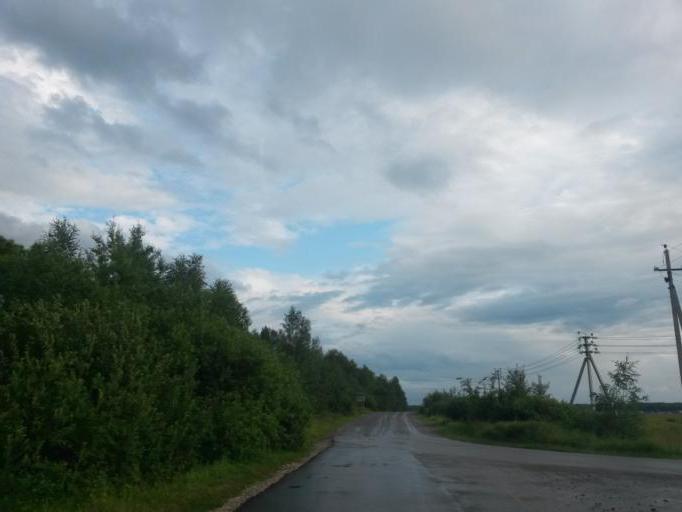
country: RU
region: Moskovskaya
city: Stolbovaya
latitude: 55.2512
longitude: 37.4611
